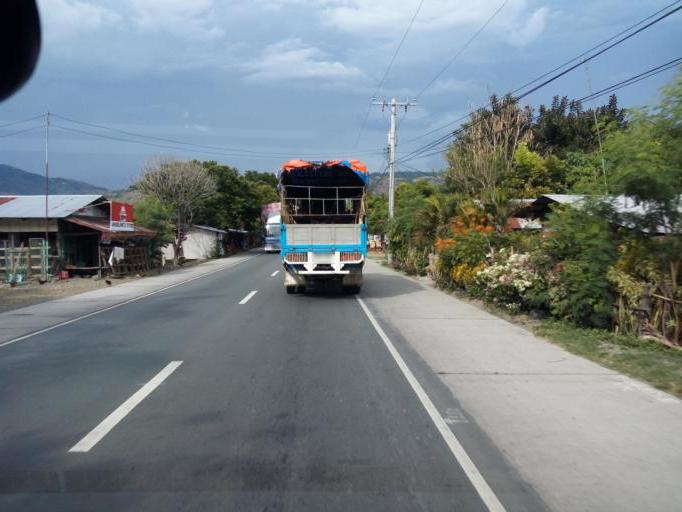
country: PH
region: Central Luzon
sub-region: Province of Nueva Ecija
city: Tayabo
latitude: 15.8275
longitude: 121.0231
